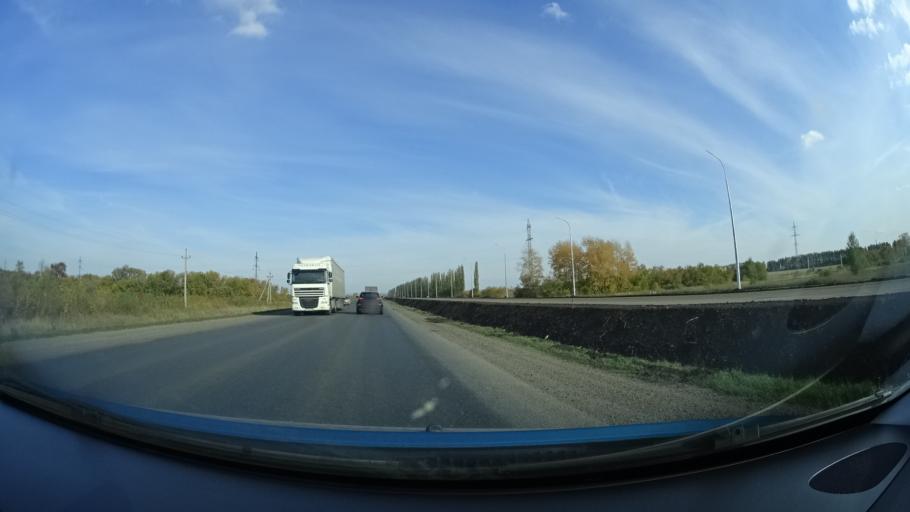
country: RU
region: Bashkortostan
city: Buzdyak
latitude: 54.6418
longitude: 54.5128
